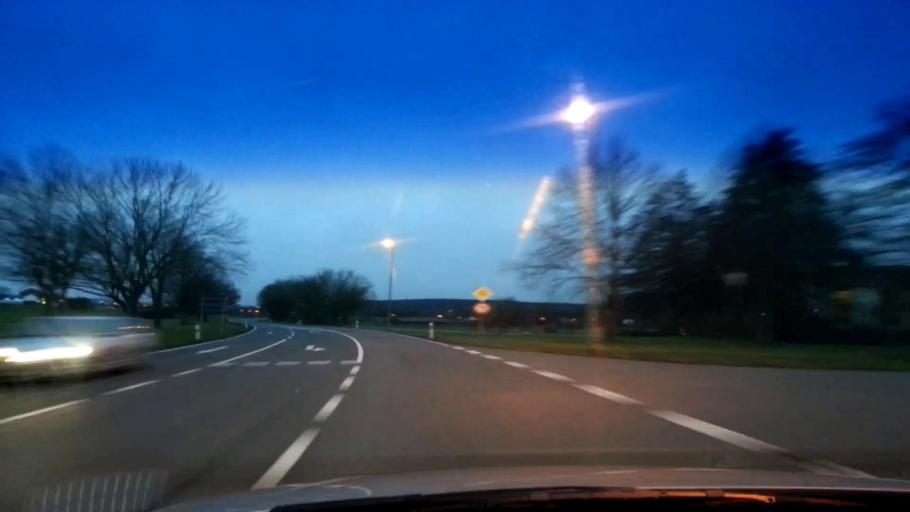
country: DE
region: Bavaria
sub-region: Upper Franconia
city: Memmelsdorf
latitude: 49.9266
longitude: 10.9566
